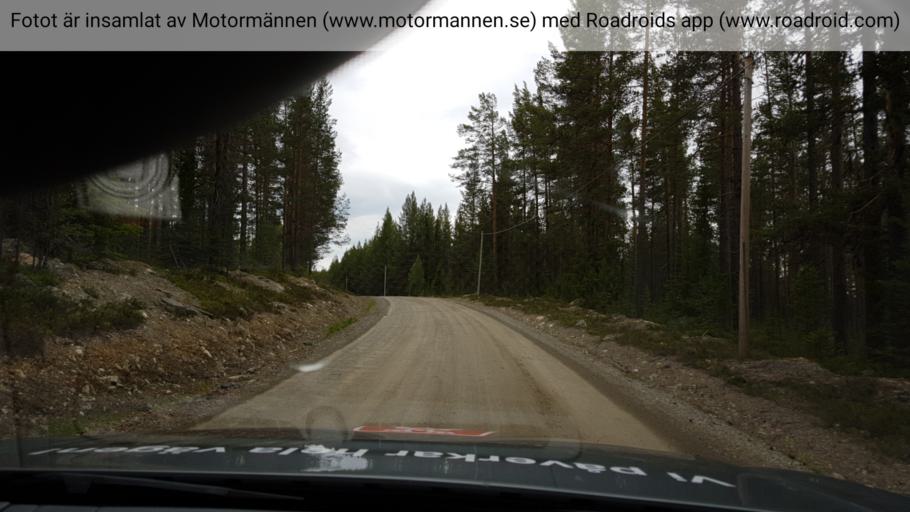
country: SE
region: Jaemtland
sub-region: Bergs Kommun
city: Hoverberg
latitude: 62.7827
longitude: 13.8244
